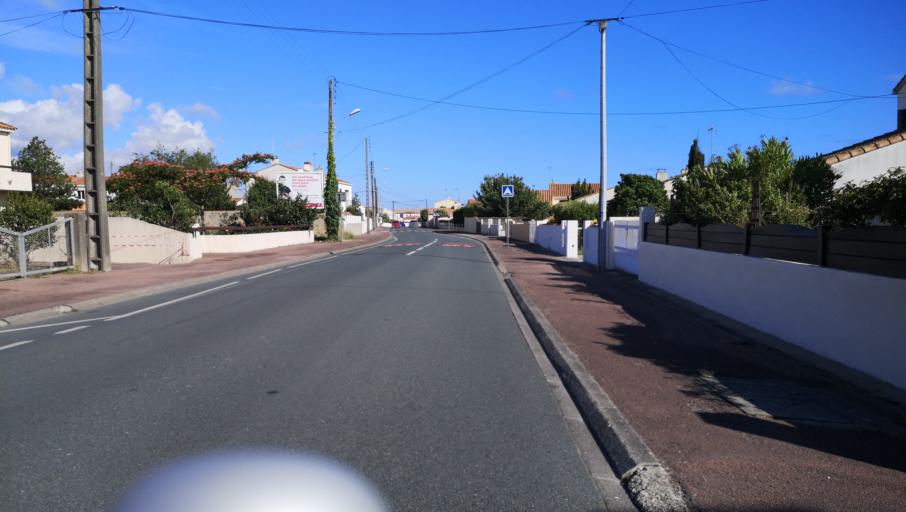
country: FR
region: Pays de la Loire
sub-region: Departement de la Vendee
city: Les Sables-d'Olonne
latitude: 46.5116
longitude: -1.7880
